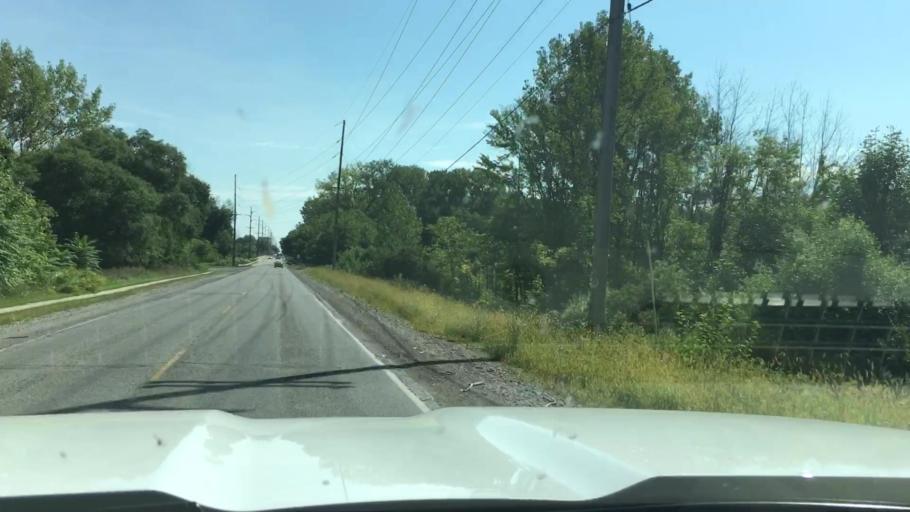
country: US
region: Michigan
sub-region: Saginaw County
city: Freeland
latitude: 43.5250
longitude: -84.1315
